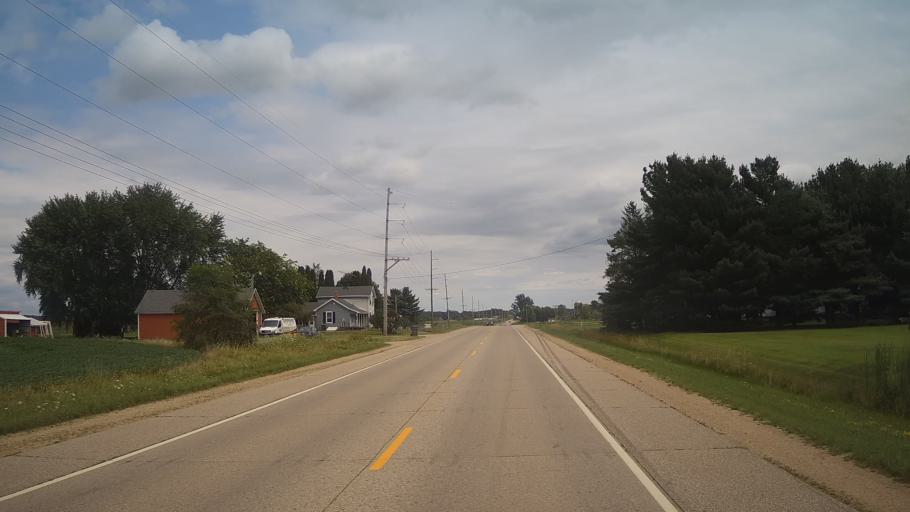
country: US
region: Wisconsin
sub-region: Waushara County
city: Redgranite
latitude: 44.0413
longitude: -89.0343
